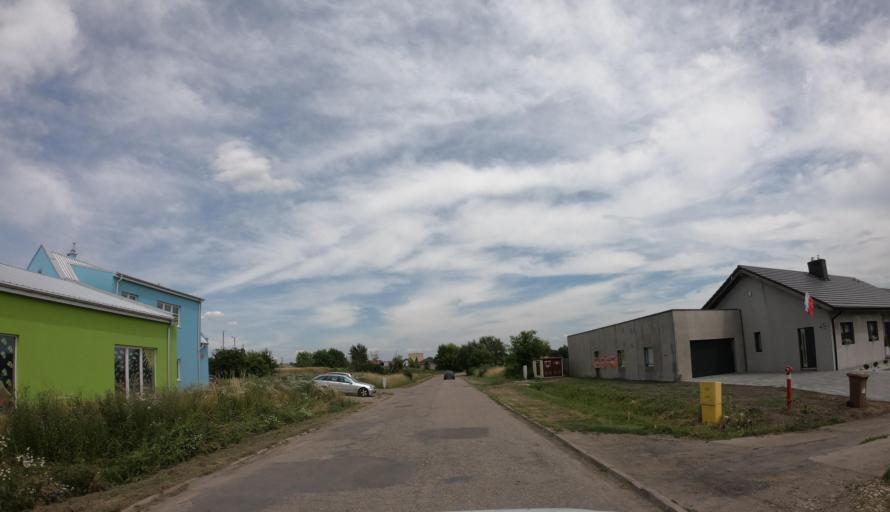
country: PL
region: West Pomeranian Voivodeship
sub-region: Powiat pyrzycki
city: Pyrzyce
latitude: 53.1435
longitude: 14.8783
